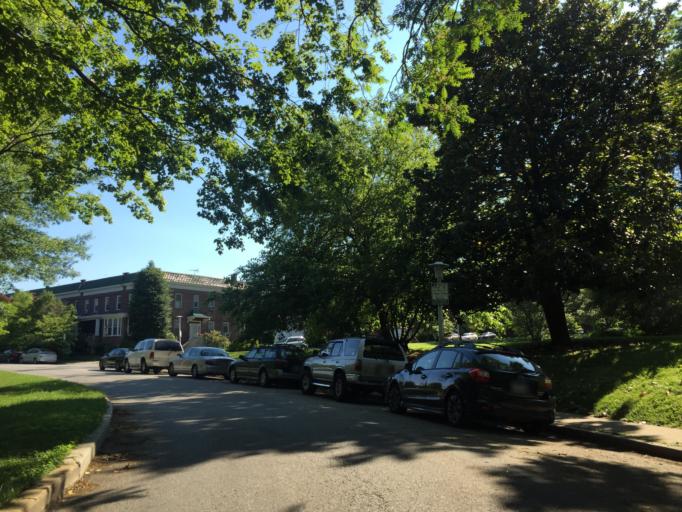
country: US
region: Maryland
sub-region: City of Baltimore
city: Baltimore
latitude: 39.3358
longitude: -76.6257
